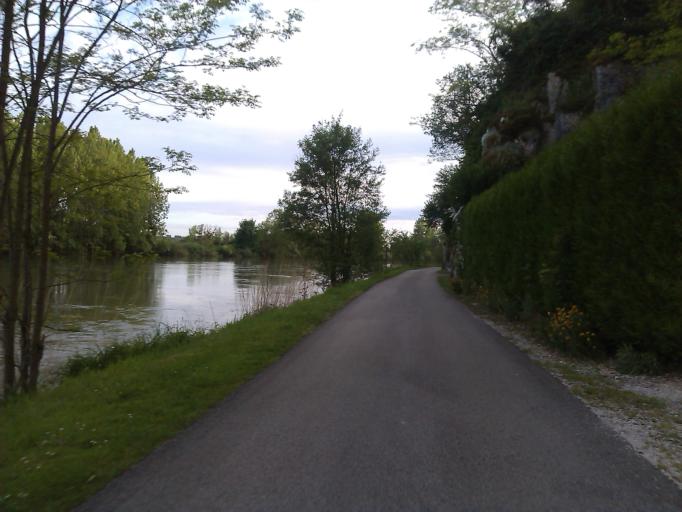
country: FR
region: Franche-Comte
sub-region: Departement du Jura
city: Dole
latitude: 47.1334
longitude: 5.5765
